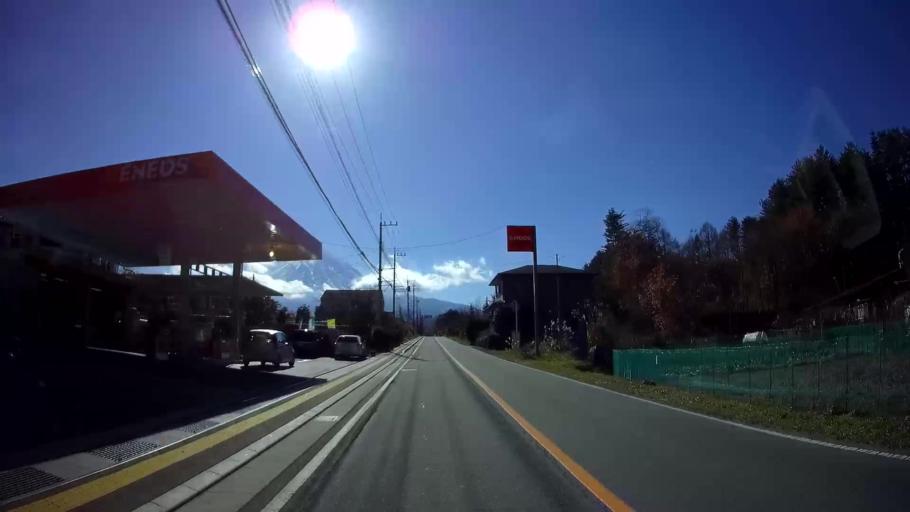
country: JP
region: Yamanashi
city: Fujikawaguchiko
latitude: 35.4918
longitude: 138.7283
